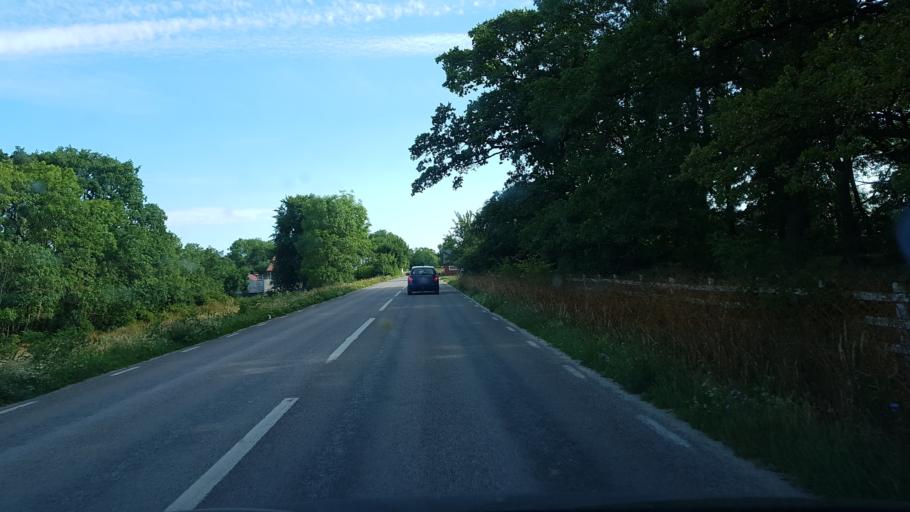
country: SE
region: Gotland
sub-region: Gotland
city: Visby
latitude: 57.7619
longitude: 18.4275
